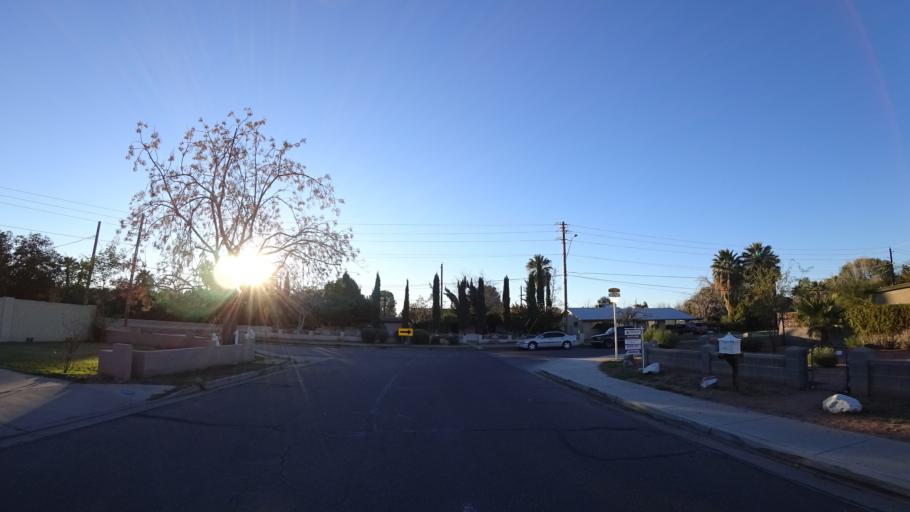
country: US
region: Arizona
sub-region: Maricopa County
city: Phoenix
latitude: 33.4740
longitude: -112.0258
